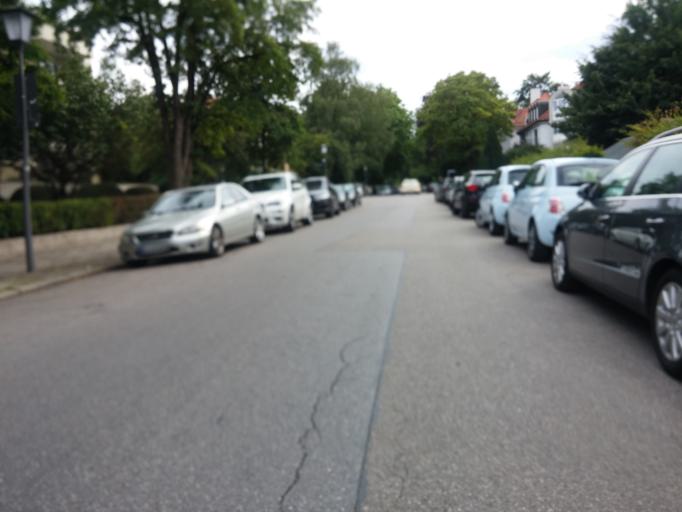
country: DE
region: Bavaria
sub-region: Upper Bavaria
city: Bogenhausen
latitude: 48.1463
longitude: 11.6020
